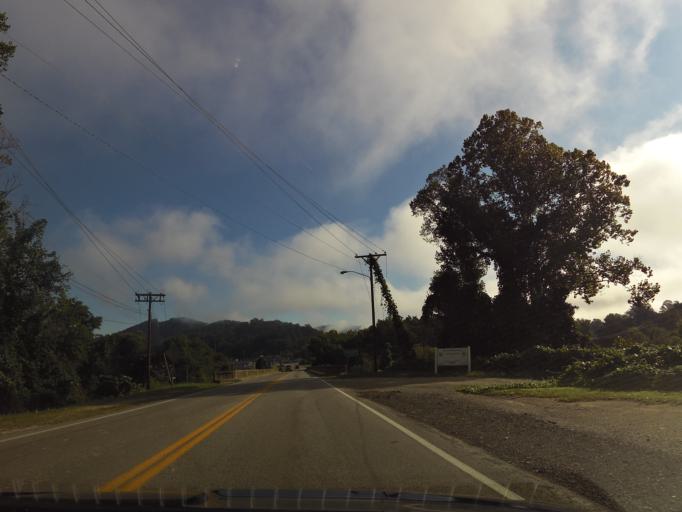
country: US
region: Kentucky
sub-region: Whitley County
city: Williamsburg
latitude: 36.7278
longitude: -84.1597
